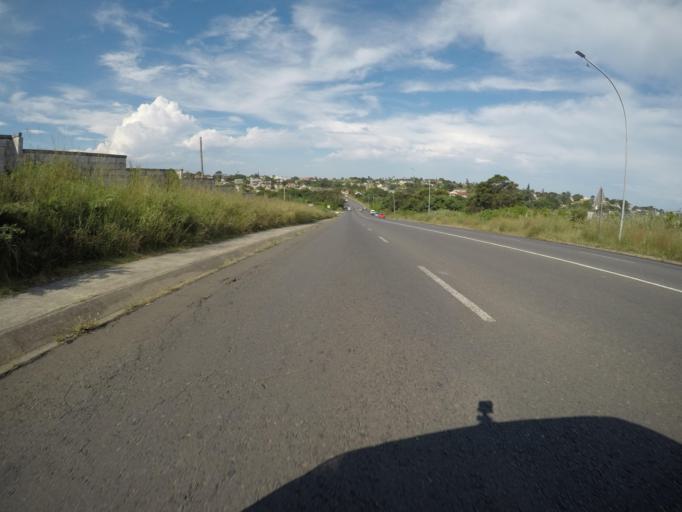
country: ZA
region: Eastern Cape
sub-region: Buffalo City Metropolitan Municipality
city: East London
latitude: -32.9938
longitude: 27.8546
